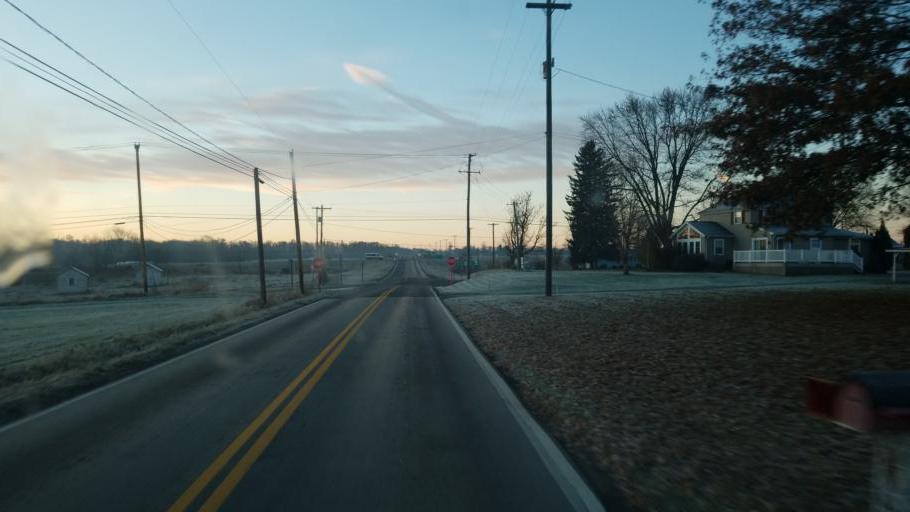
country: US
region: Ohio
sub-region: Wayne County
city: Orrville
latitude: 40.7972
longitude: -81.7850
